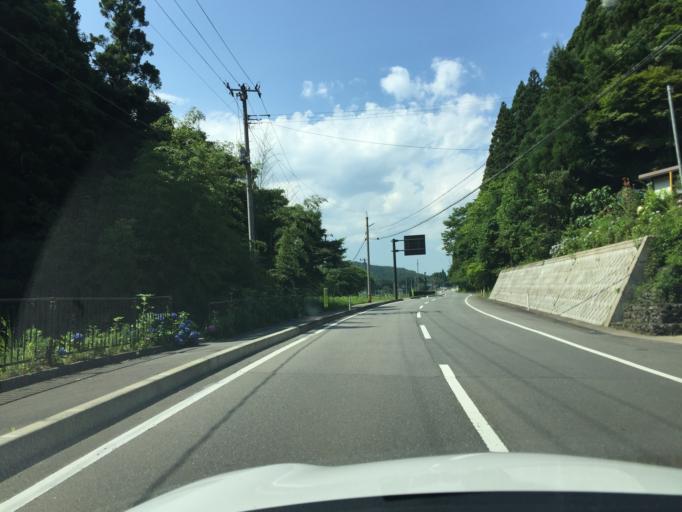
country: JP
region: Ibaraki
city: Kitaibaraki
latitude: 36.9575
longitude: 140.7040
